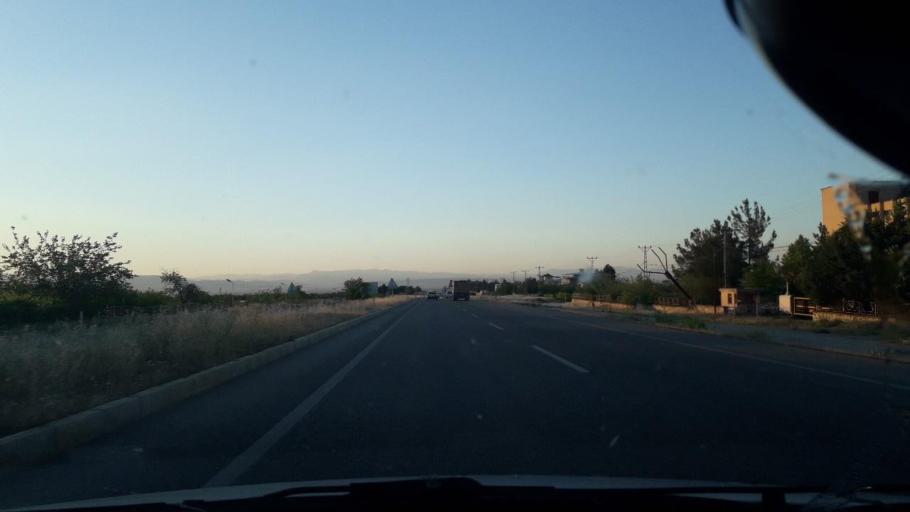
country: TR
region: Malatya
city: Yesilyurt
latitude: 38.3943
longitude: 38.2238
